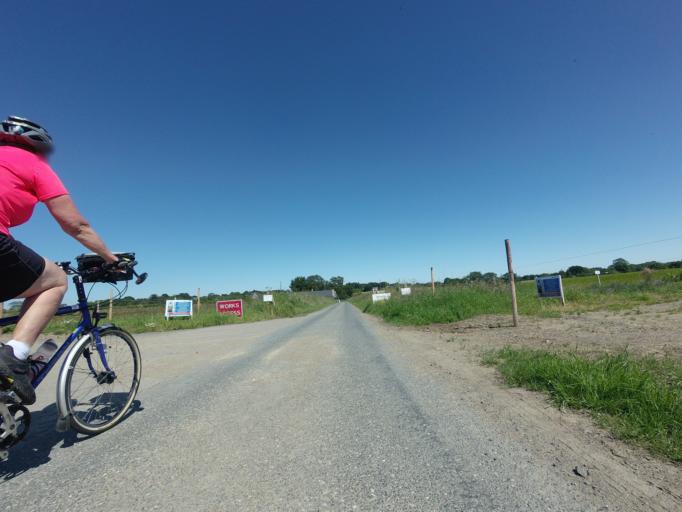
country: GB
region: Scotland
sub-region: Aberdeenshire
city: Macduff
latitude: 57.6305
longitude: -2.4850
